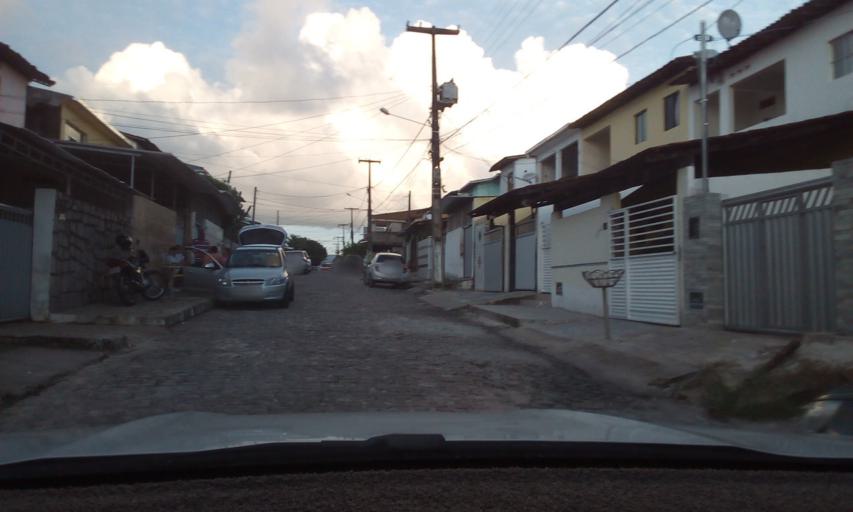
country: BR
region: Paraiba
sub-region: Joao Pessoa
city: Joao Pessoa
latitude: -7.1782
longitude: -34.8432
